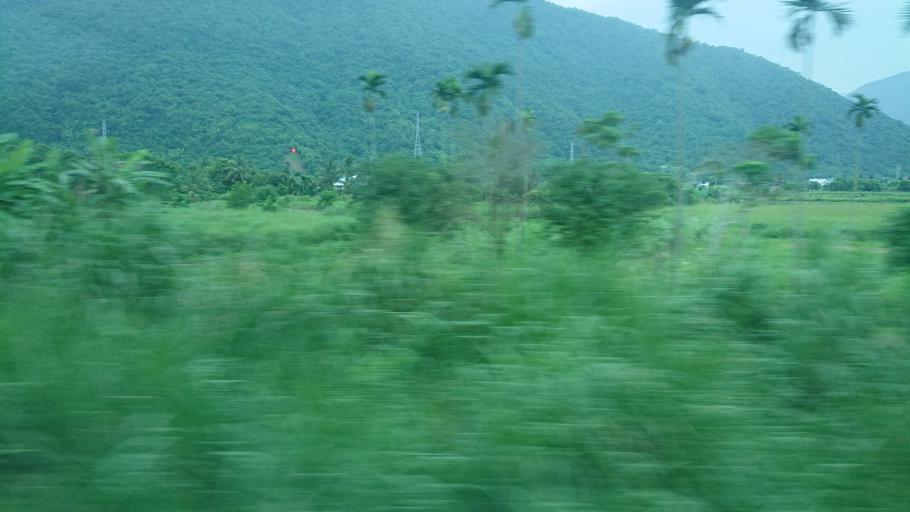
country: TW
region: Taiwan
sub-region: Hualien
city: Hualian
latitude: 24.1185
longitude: 121.6319
